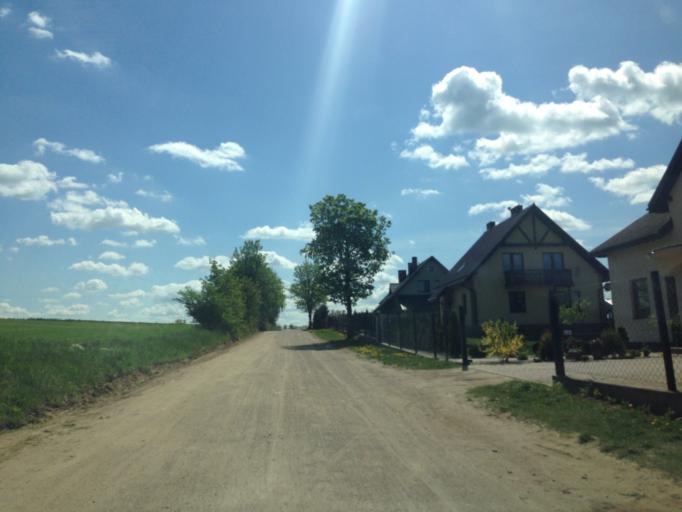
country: PL
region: Kujawsko-Pomorskie
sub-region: Powiat brodnicki
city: Brzozie
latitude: 53.3217
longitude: 19.6117
